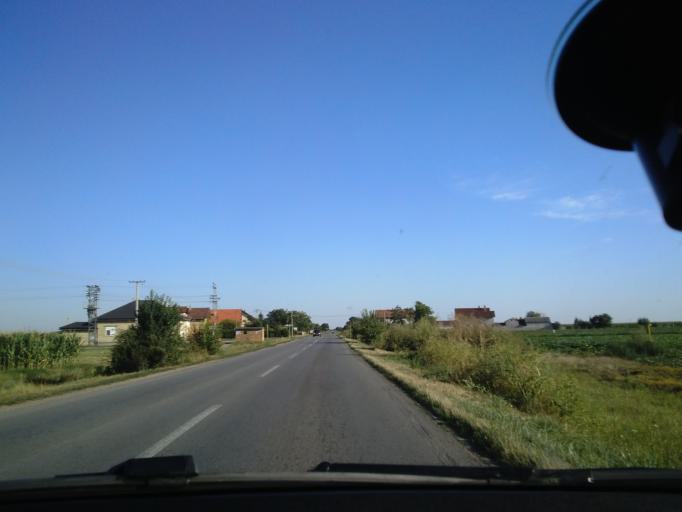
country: RS
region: Autonomna Pokrajina Vojvodina
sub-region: Zapadnobacki Okrug
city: Sombor
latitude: 45.7103
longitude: 19.1630
